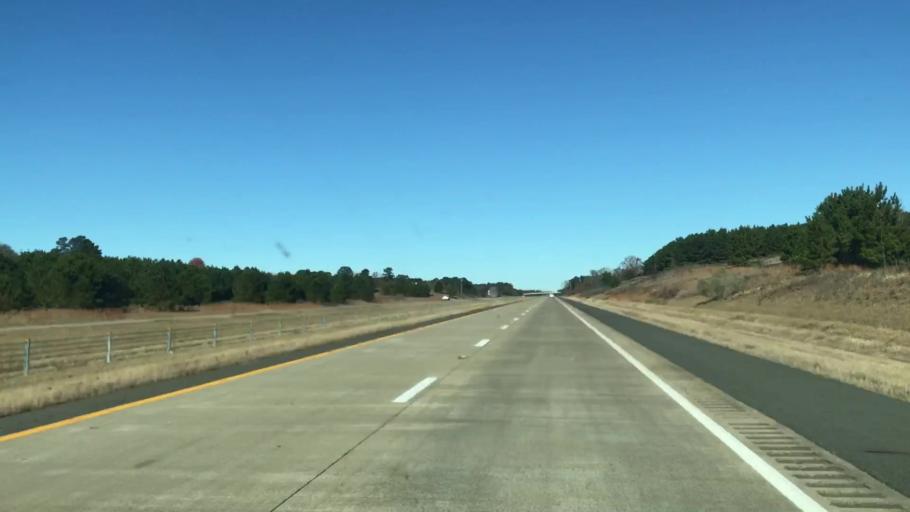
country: US
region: Texas
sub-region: Bowie County
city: Texarkana
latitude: 33.2800
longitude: -93.9082
